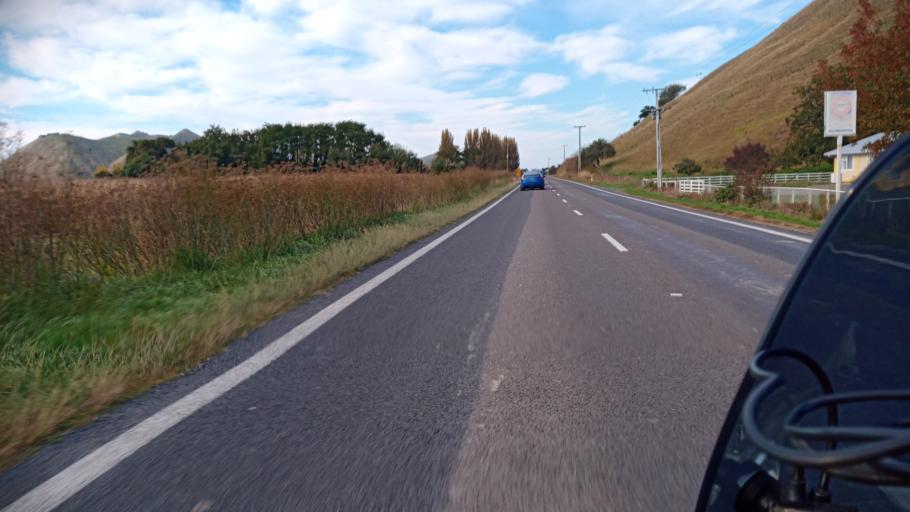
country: NZ
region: Gisborne
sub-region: Gisborne District
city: Gisborne
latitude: -38.7517
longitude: 177.9221
